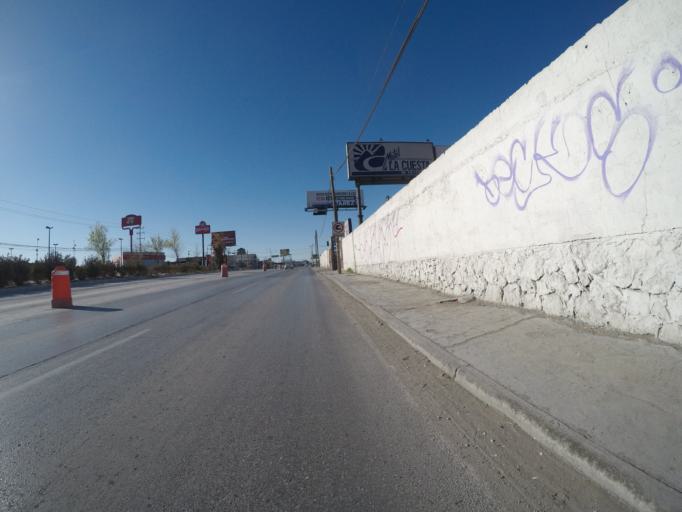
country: MX
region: Chihuahua
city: Ciudad Juarez
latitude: 31.6768
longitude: -106.4248
